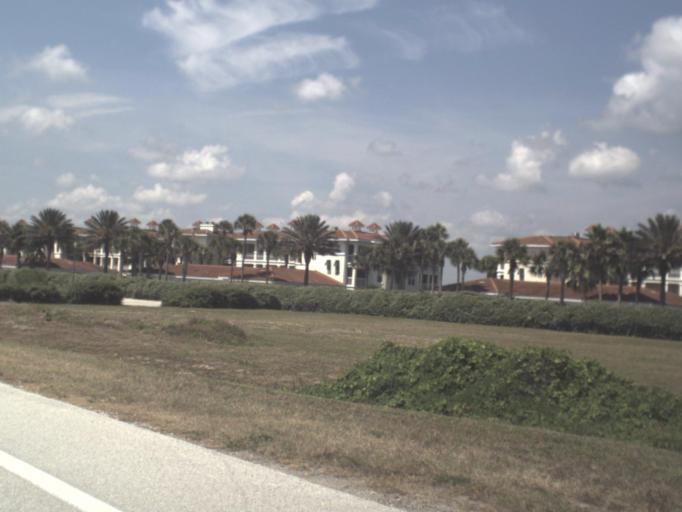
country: US
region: Florida
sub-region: Saint Johns County
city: Villano Beach
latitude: 29.9701
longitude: -81.3109
